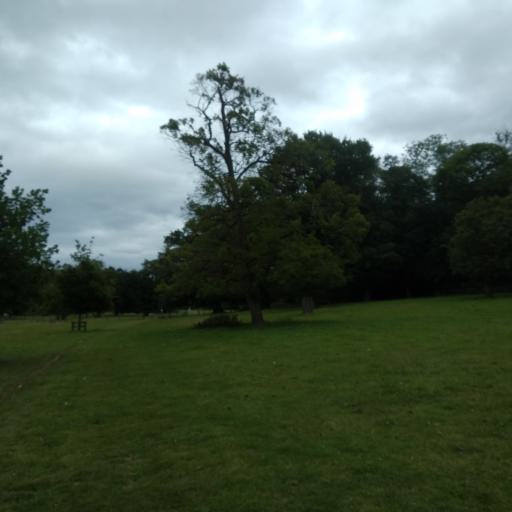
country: GB
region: England
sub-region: Kent
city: Ashford
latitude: 51.1627
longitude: 0.8388
